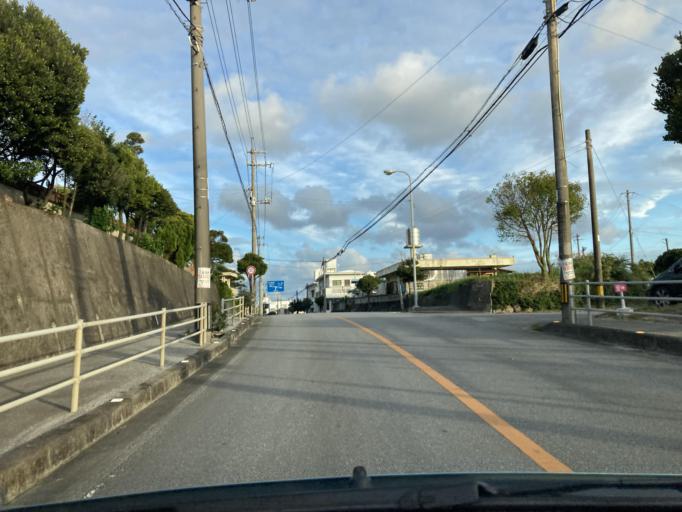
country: JP
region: Okinawa
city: Tomigusuku
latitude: 26.1511
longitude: 127.7053
